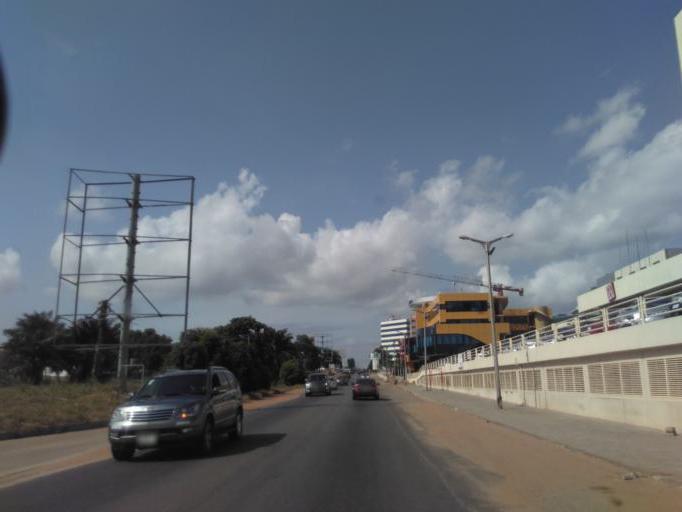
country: GH
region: Greater Accra
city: Accra
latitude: 5.6034
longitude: -0.1757
